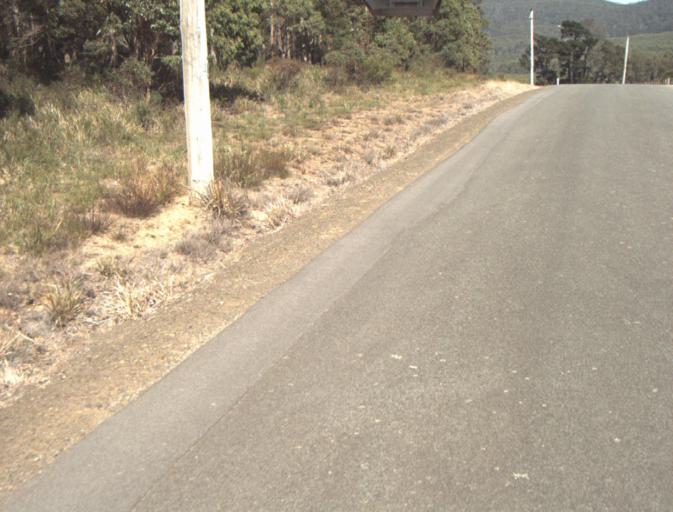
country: AU
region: Tasmania
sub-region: Launceston
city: Newstead
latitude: -41.3188
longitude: 147.3269
